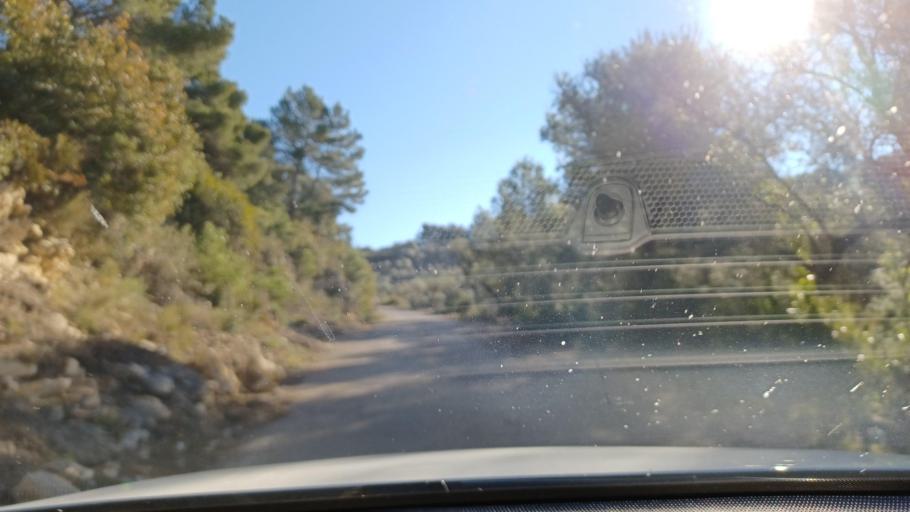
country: ES
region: Catalonia
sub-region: Provincia de Tarragona
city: Tortosa
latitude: 40.8170
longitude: 0.5681
